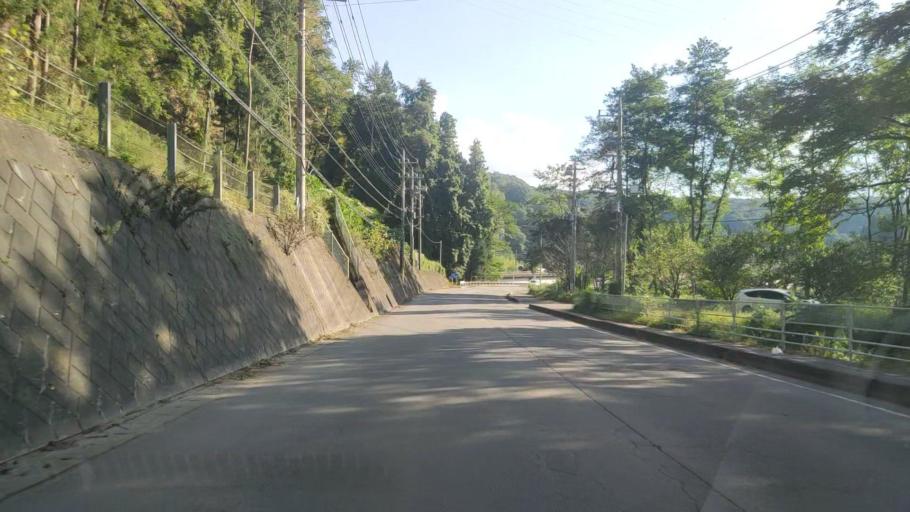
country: JP
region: Nagano
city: Komoro
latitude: 36.5251
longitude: 138.5432
